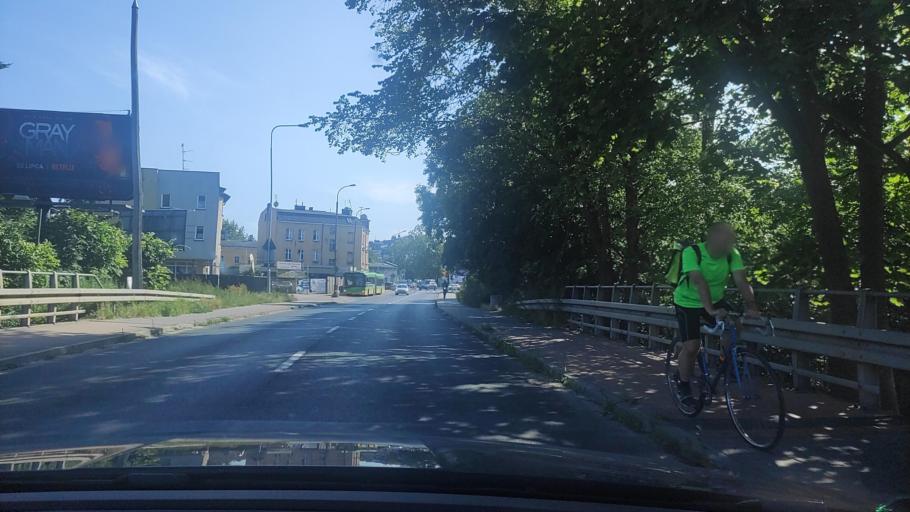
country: PL
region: Greater Poland Voivodeship
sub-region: Powiat poznanski
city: Czerwonak
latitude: 52.4236
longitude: 16.9769
